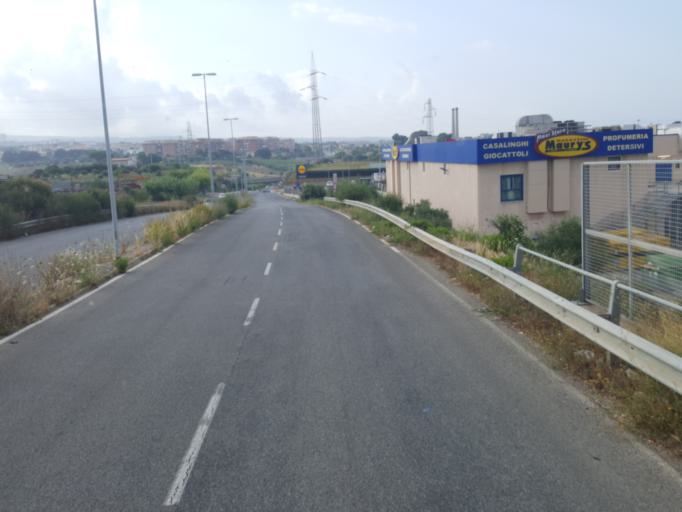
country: IT
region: Latium
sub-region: Citta metropolitana di Roma Capitale
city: Civitavecchia
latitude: 42.1084
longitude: 11.7866
